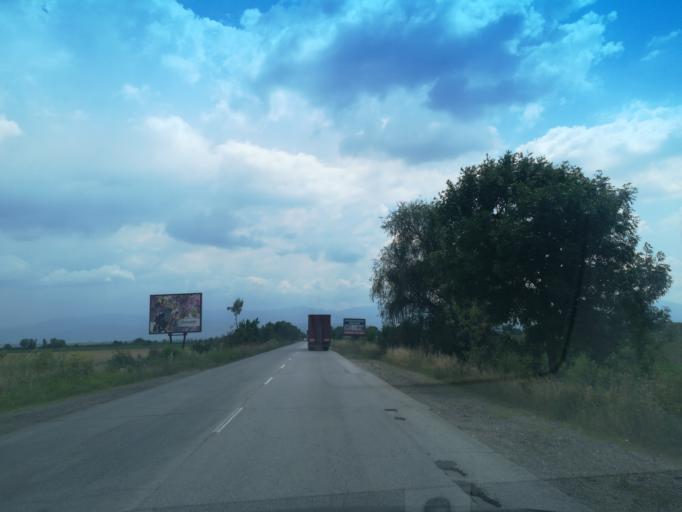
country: BG
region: Plovdiv
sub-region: Obshtina Plovdiv
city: Plovdiv
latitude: 42.1820
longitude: 24.6765
